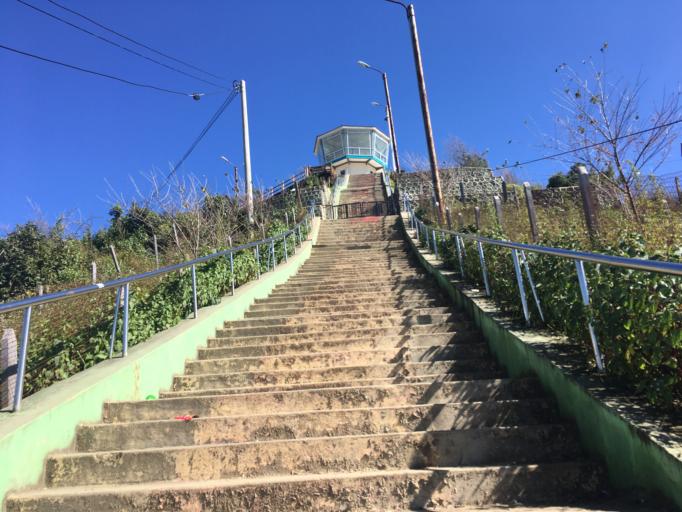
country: MM
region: Chin
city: Hakha
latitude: 22.6376
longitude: 93.6068
